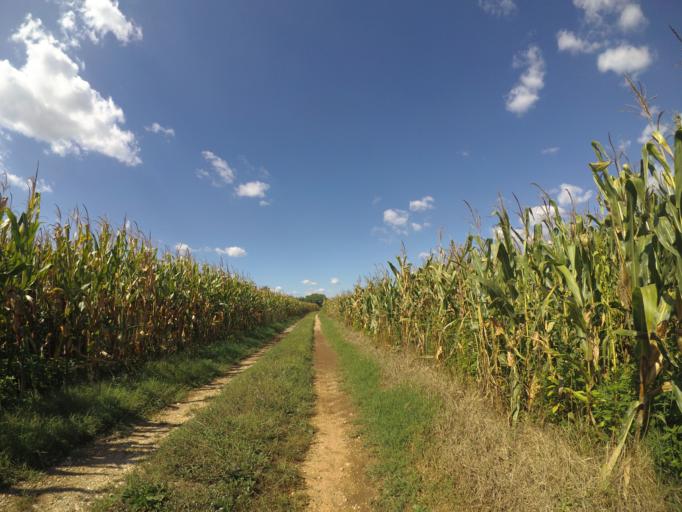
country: IT
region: Friuli Venezia Giulia
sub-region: Provincia di Udine
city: Talmassons
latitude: 45.9288
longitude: 13.1338
